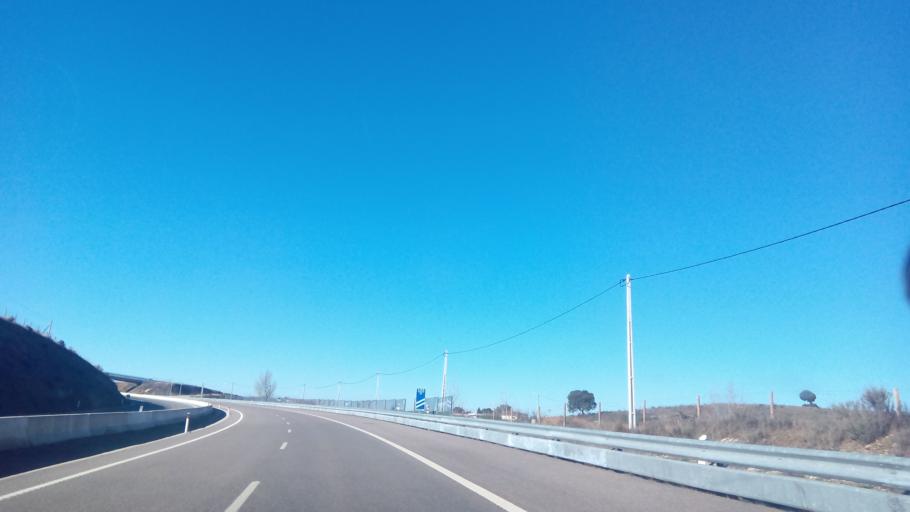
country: PT
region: Braganca
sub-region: Braganca Municipality
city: Braganca
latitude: 41.7894
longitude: -6.7102
